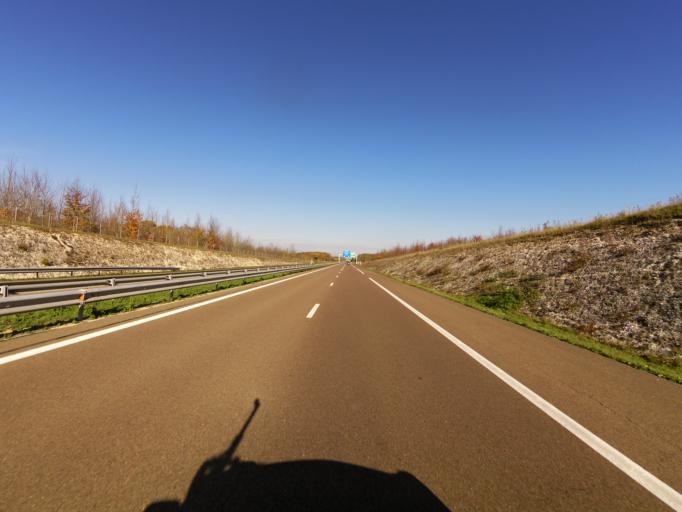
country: FR
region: Champagne-Ardenne
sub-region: Departement de la Marne
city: Fagnieres
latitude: 48.9002
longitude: 4.2858
